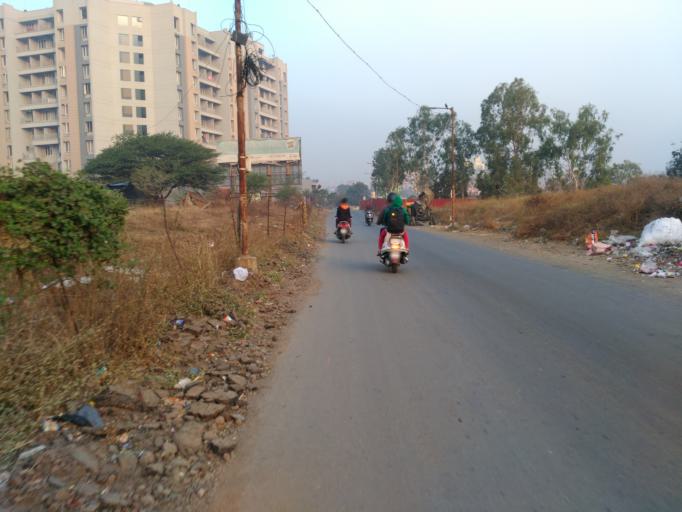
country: IN
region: Maharashtra
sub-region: Pune Division
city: Pune
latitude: 18.4489
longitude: 73.8849
